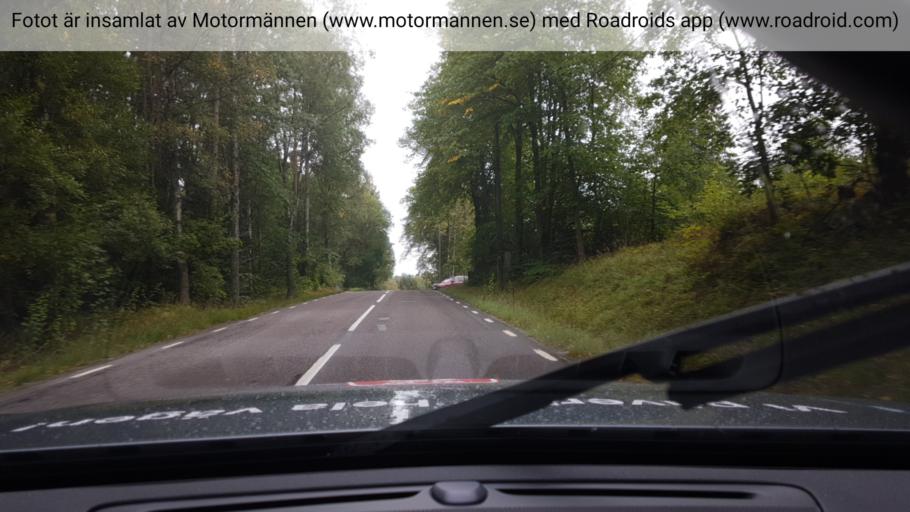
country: SE
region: Stockholm
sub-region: Botkyrka Kommun
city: Varsta
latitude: 59.1084
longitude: 17.8725
